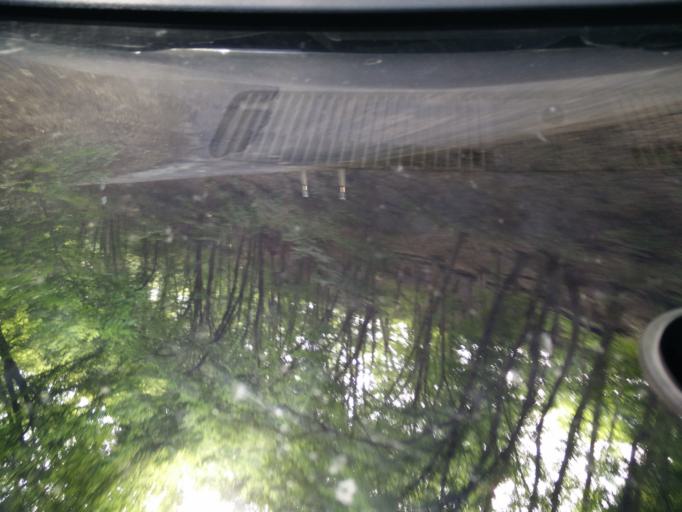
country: HU
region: Komarom-Esztergom
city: Tardos
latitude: 47.6964
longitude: 18.4460
